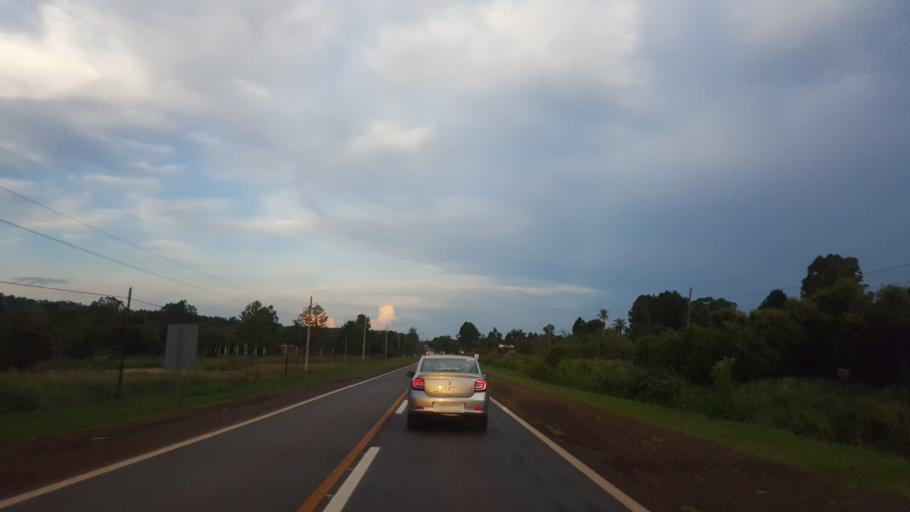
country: AR
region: Misiones
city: Jardin America
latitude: -27.0314
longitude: -55.2194
